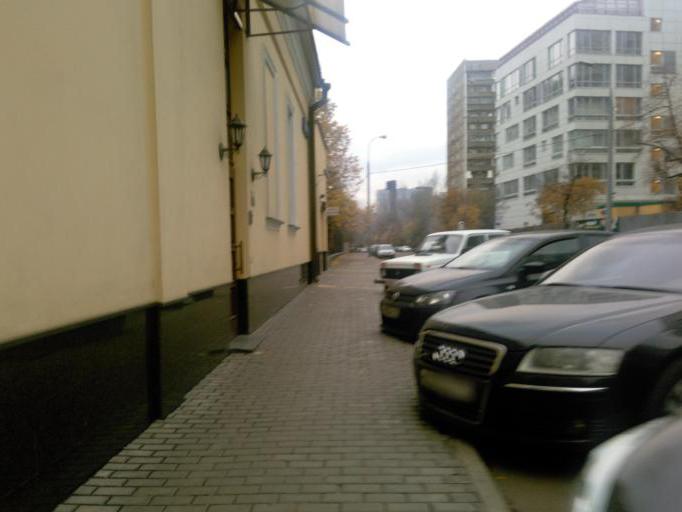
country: RU
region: Moskovskaya
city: Dorogomilovo
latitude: 55.7298
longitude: 37.5750
